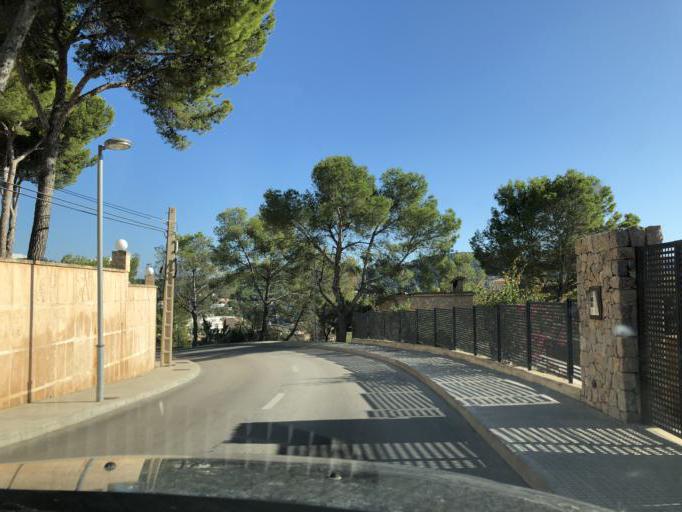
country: ES
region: Balearic Islands
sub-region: Illes Balears
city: Camp de Mar
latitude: 39.5412
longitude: 2.4148
